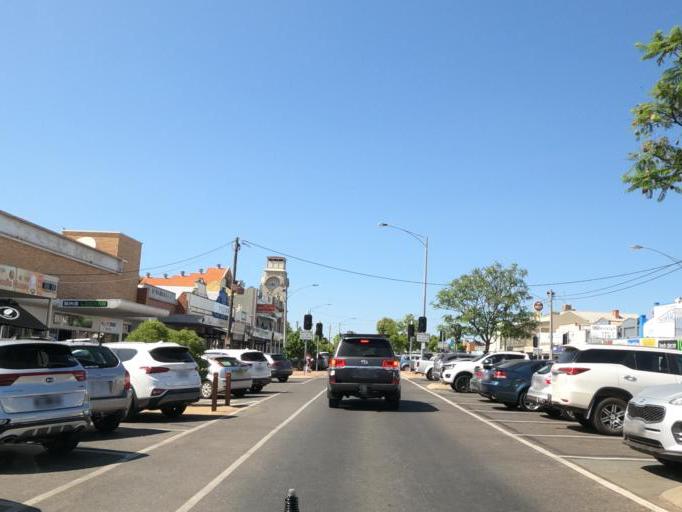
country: AU
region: Victoria
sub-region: Moira
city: Yarrawonga
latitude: -36.0117
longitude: 146.0045
